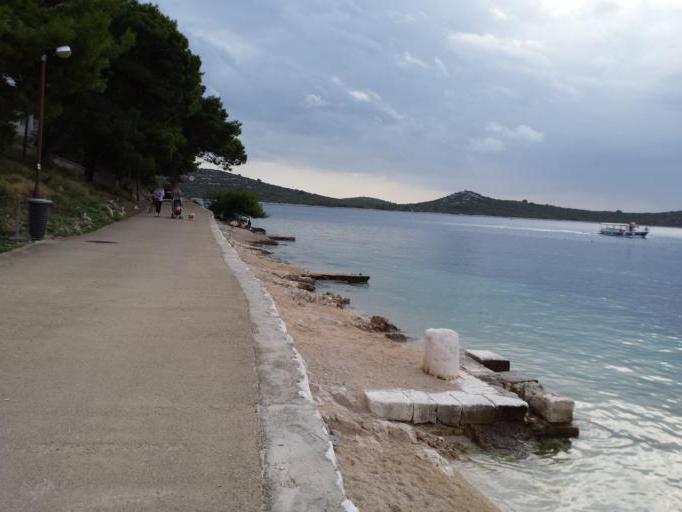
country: HR
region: Sibensko-Kniniska
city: Rogoznica
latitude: 43.5231
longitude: 15.9679
